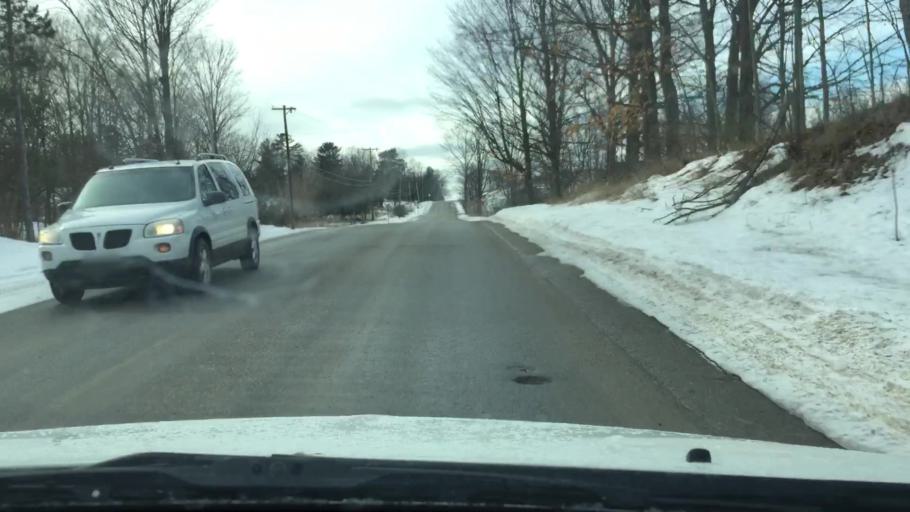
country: US
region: Michigan
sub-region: Wexford County
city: Manton
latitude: 44.4037
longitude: -85.4044
